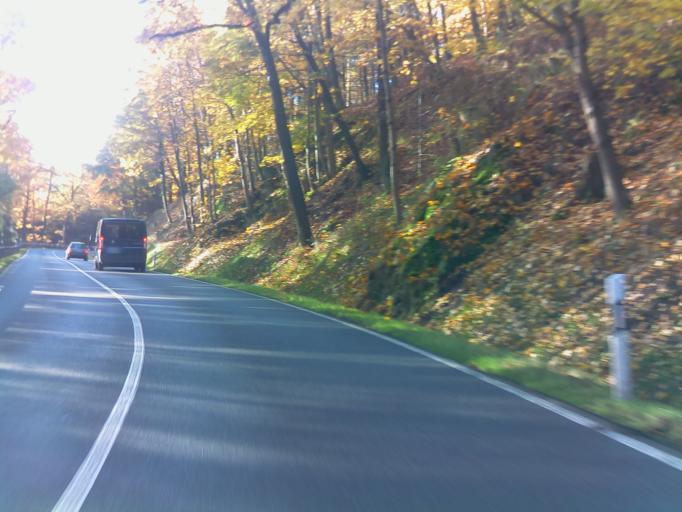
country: DE
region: Thuringia
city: Saalfeld
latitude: 50.6211
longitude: 11.3289
